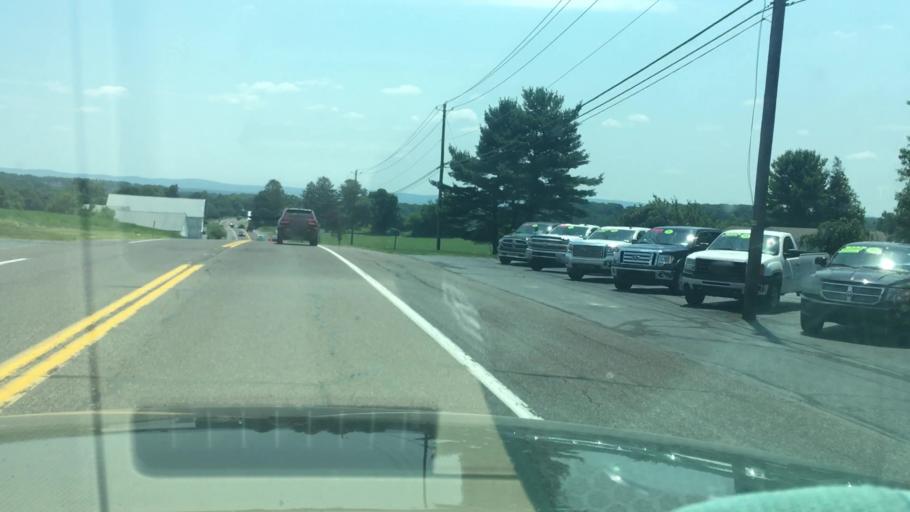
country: US
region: Pennsylvania
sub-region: Lehigh County
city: Schnecksville
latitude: 40.6112
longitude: -75.6498
